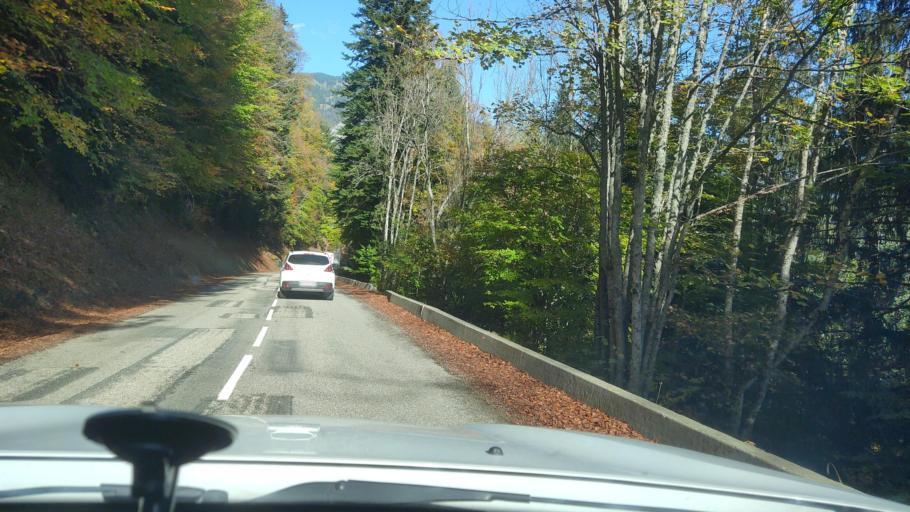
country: FR
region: Rhone-Alpes
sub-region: Departement de la Savoie
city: Ugine
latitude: 45.7828
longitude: 6.4815
